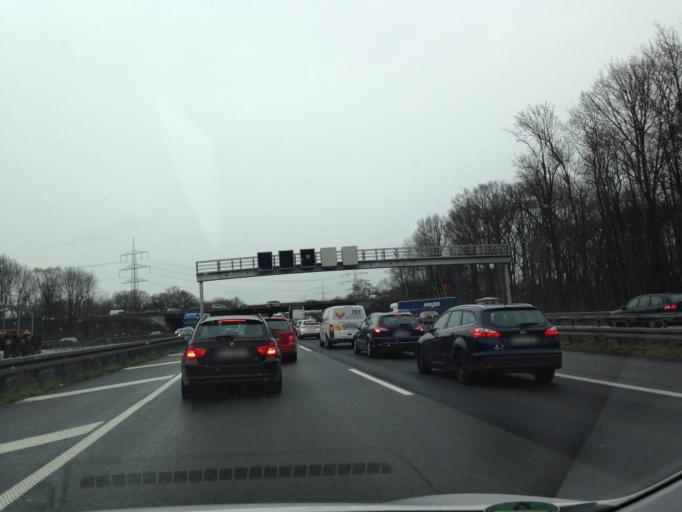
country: DE
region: North Rhine-Westphalia
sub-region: Regierungsbezirk Dusseldorf
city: Meerbusch
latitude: 51.2895
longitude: 6.6355
